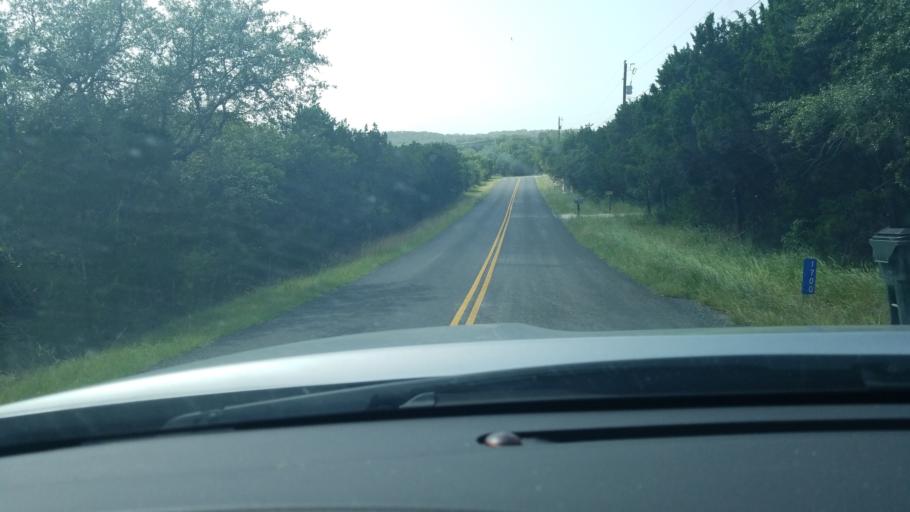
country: US
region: Texas
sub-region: Comal County
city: Bulverde
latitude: 29.7955
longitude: -98.4422
